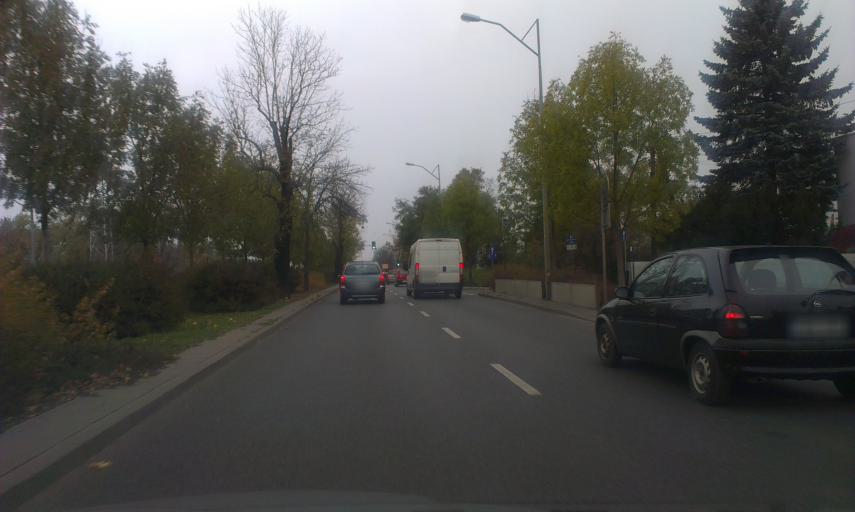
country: PL
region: Greater Poland Voivodeship
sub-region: Powiat poznanski
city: Suchy Las
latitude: 52.4154
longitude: 16.8704
